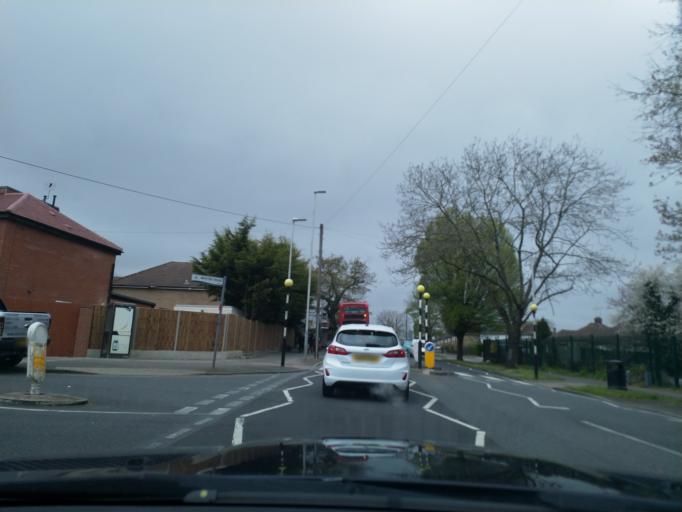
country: GB
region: England
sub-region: Greater London
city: Pinner
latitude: 51.5692
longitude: -0.3896
